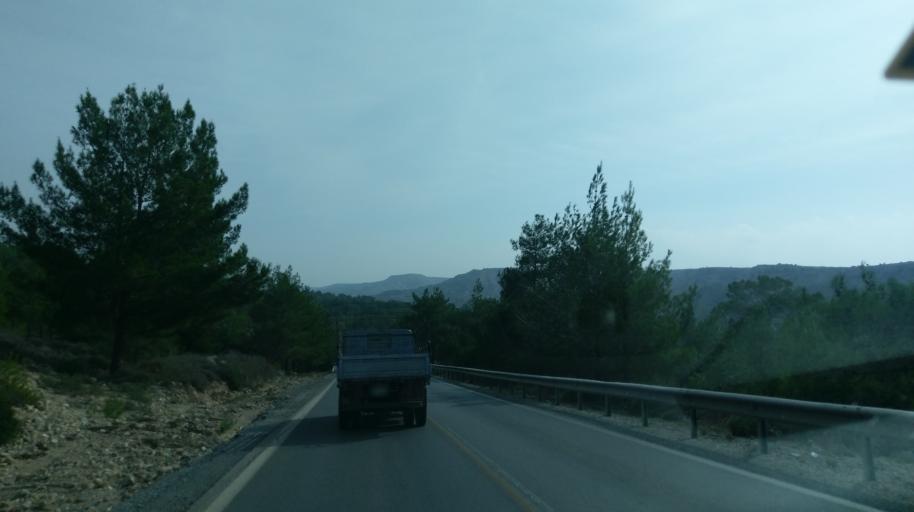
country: CY
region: Lefkosia
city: Morfou
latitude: 35.2588
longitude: 33.0384
